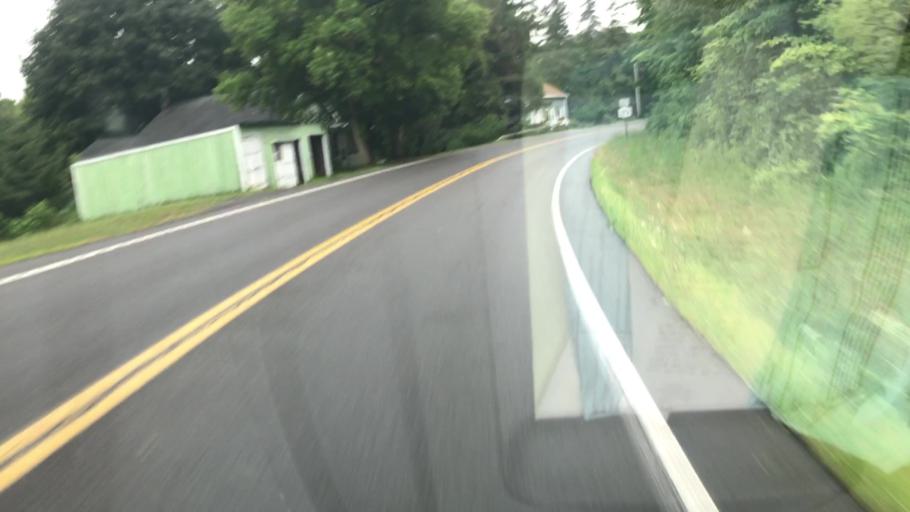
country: US
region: New York
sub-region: Onondaga County
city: Manlius
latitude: 42.9985
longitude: -75.9890
